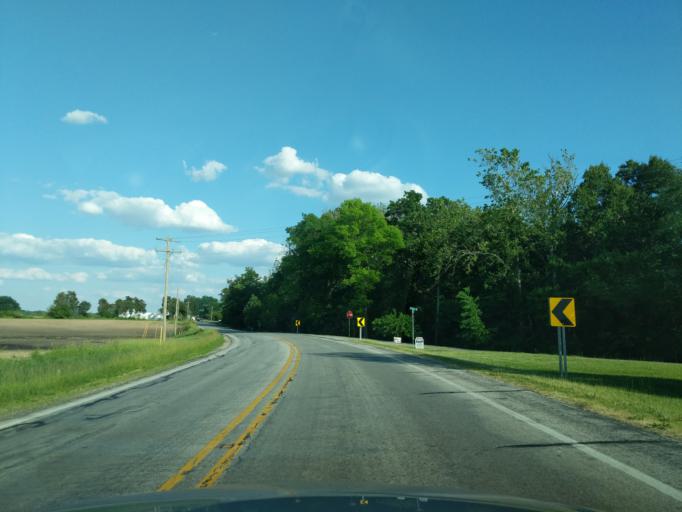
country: US
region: Indiana
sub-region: Whitley County
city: Tri-Lakes
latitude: 41.2832
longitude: -85.5000
